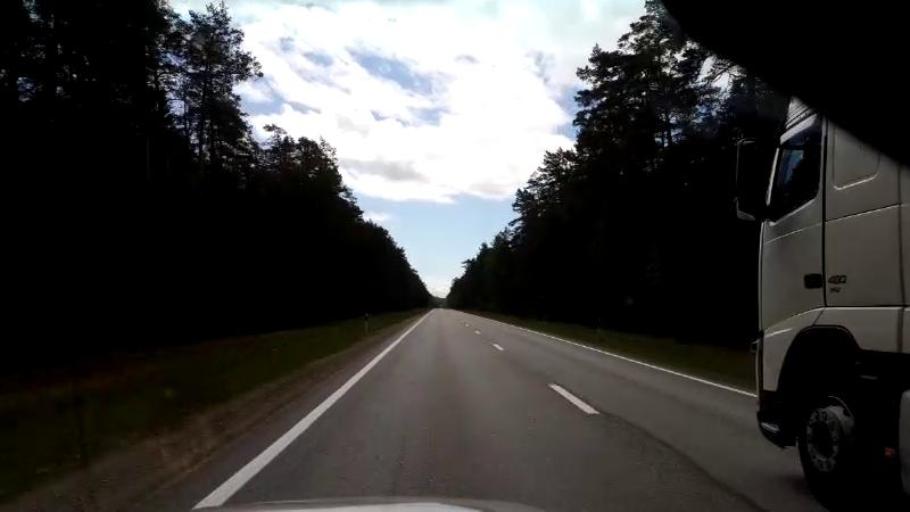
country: LV
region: Salacgrivas
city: Salacgriva
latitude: 57.5167
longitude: 24.4307
